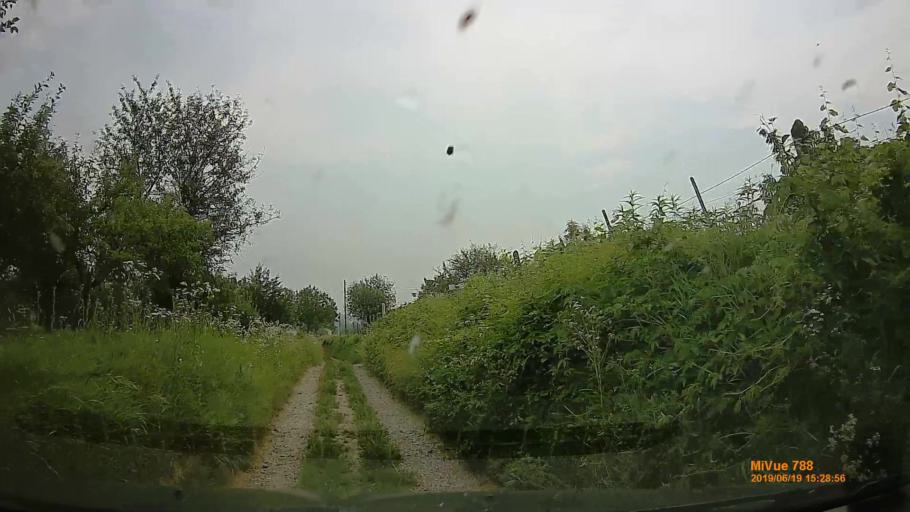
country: HU
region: Baranya
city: Szigetvar
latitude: 46.0699
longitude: 17.8479
